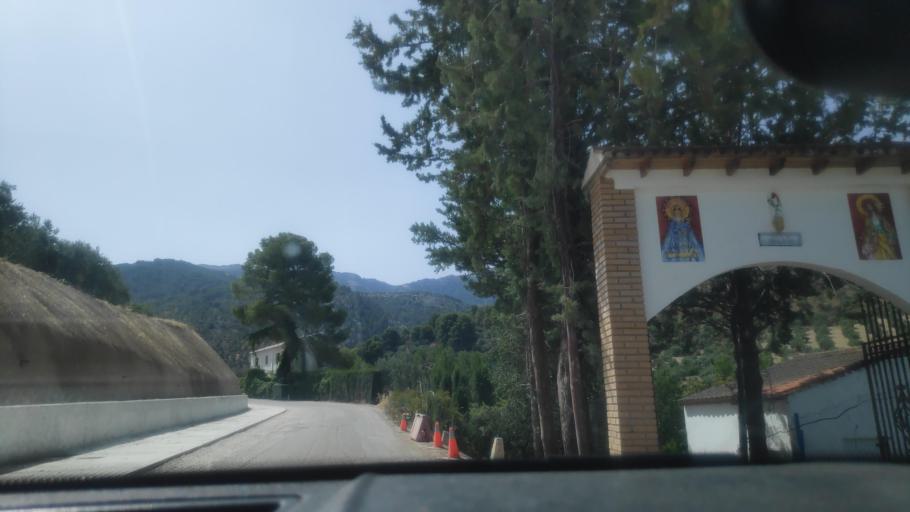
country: ES
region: Andalusia
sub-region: Provincia de Jaen
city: Jodar
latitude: 37.7991
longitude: -3.4109
